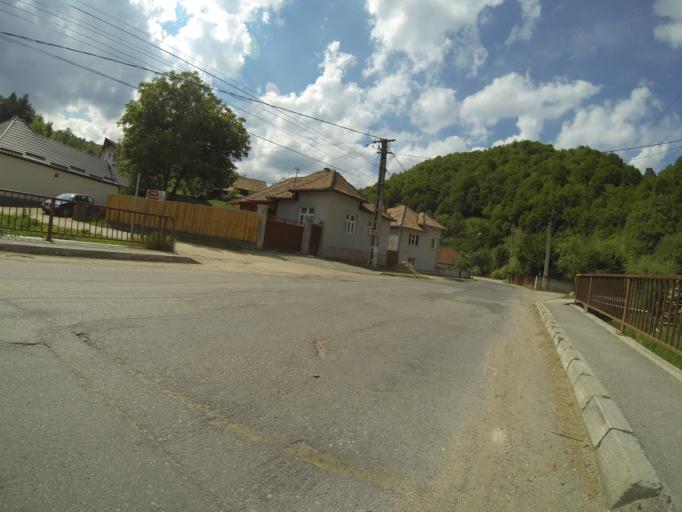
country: RO
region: Brasov
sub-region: Comuna Poiana Marului
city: Poiana Marului
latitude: 45.6081
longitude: 25.3028
